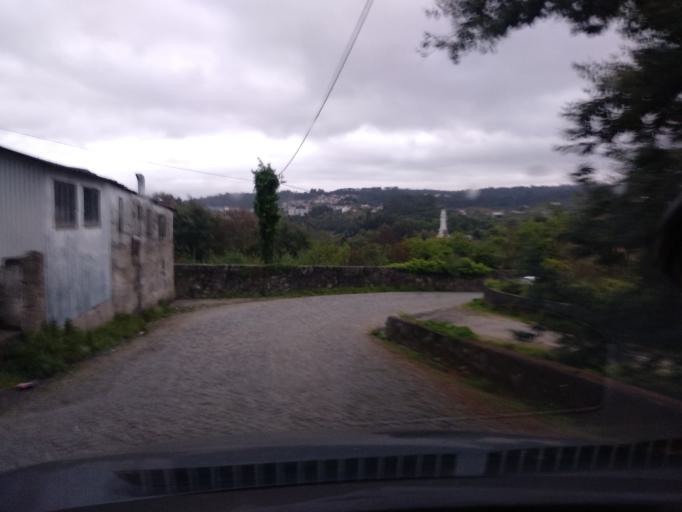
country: PT
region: Porto
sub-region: Penafiel
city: Penafiel
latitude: 41.2011
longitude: -8.2861
